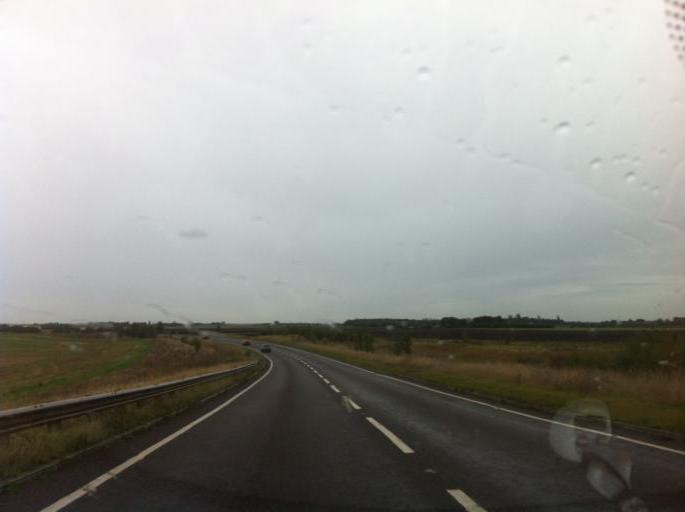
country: GB
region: England
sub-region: Peterborough
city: Eye
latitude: 52.6150
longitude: -0.2094
